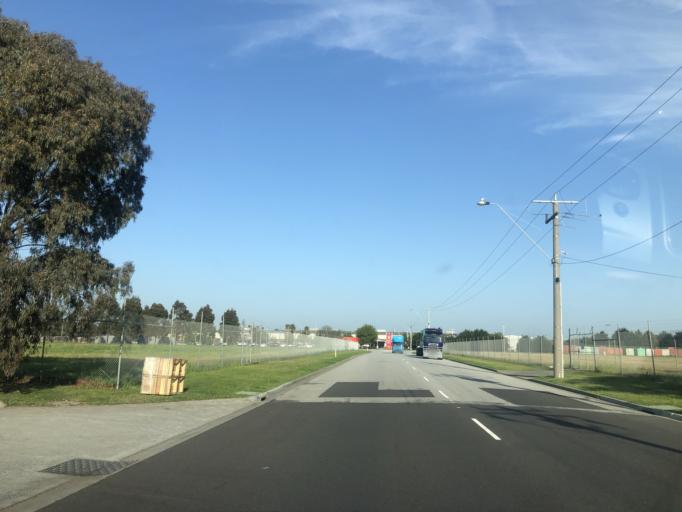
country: AU
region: Victoria
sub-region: Casey
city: Eumemmerring
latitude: -38.0112
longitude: 145.2419
